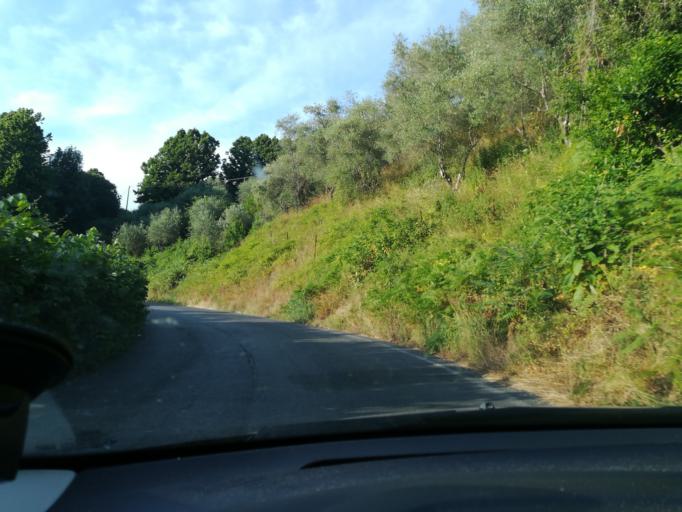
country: IT
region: Tuscany
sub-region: Provincia di Lucca
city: Stiava
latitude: 43.9160
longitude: 10.3391
